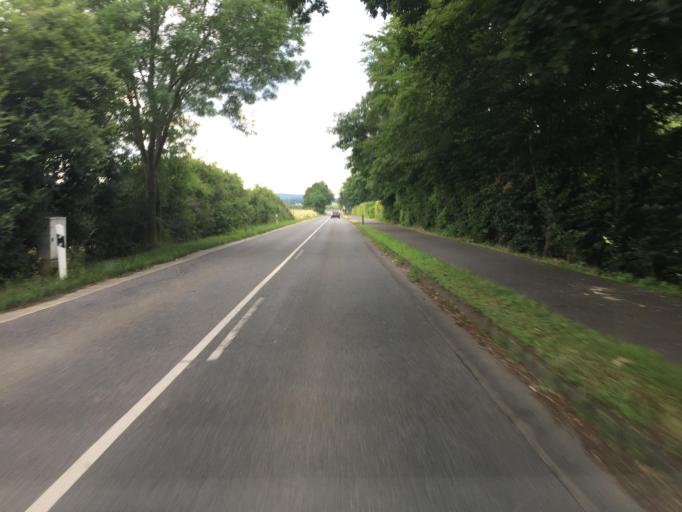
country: DE
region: North Rhine-Westphalia
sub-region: Regierungsbezirk Koln
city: Euskirchen
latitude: 50.6407
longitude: 6.7937
